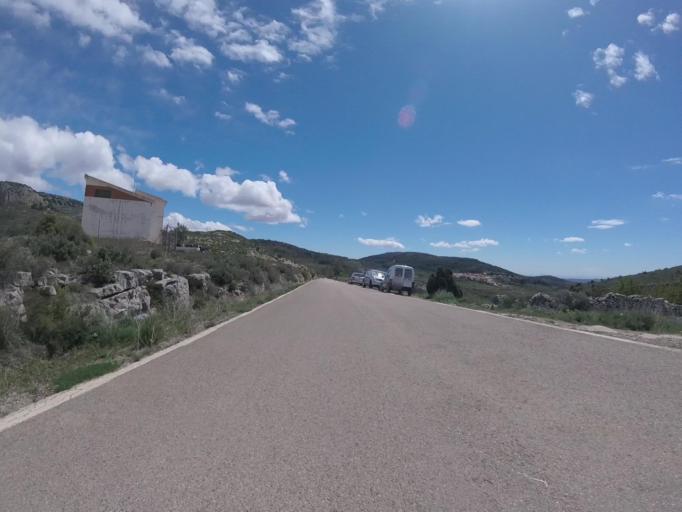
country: ES
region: Valencia
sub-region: Provincia de Castello
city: Sierra-Engarceran
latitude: 40.2758
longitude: -0.0324
